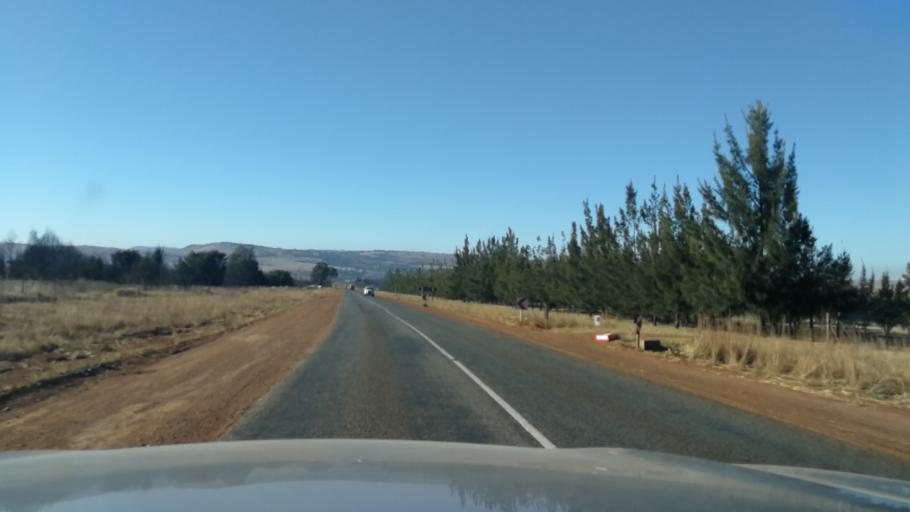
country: ZA
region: Gauteng
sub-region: West Rand District Municipality
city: Krugersdorp
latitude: -26.0014
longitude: 27.7026
